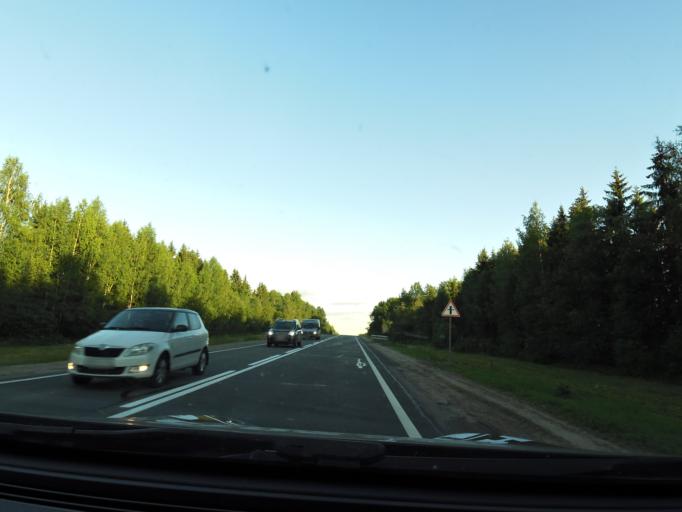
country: RU
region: Vologda
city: Gryazovets
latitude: 58.6748
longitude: 40.3092
